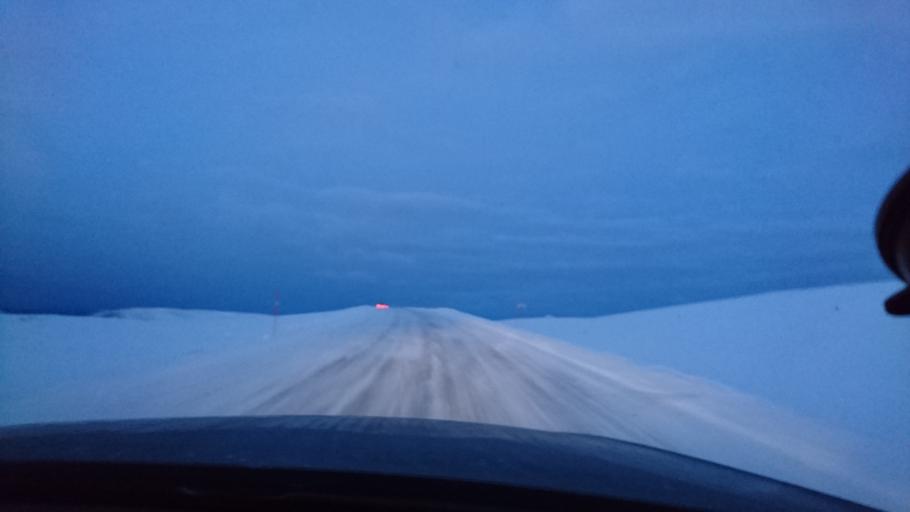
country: NO
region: Finnmark Fylke
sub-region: Nordkapp
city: Honningsvag
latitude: 71.0532
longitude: 25.7654
